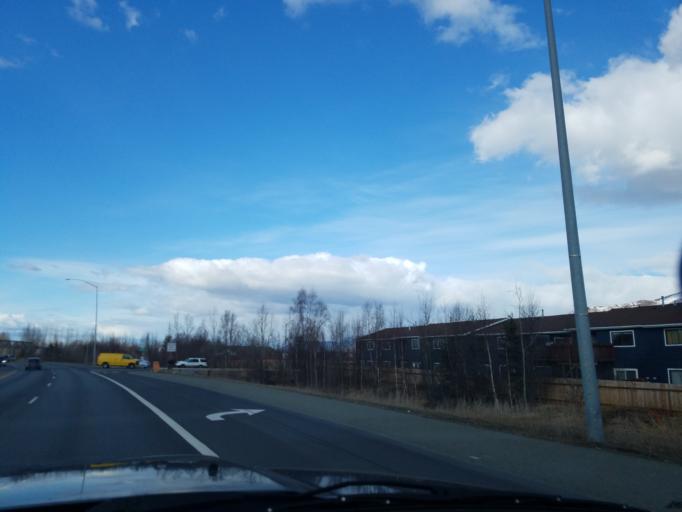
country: US
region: Alaska
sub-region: Anchorage Municipality
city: Elmendorf Air Force Base
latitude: 61.1851
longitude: -149.7337
